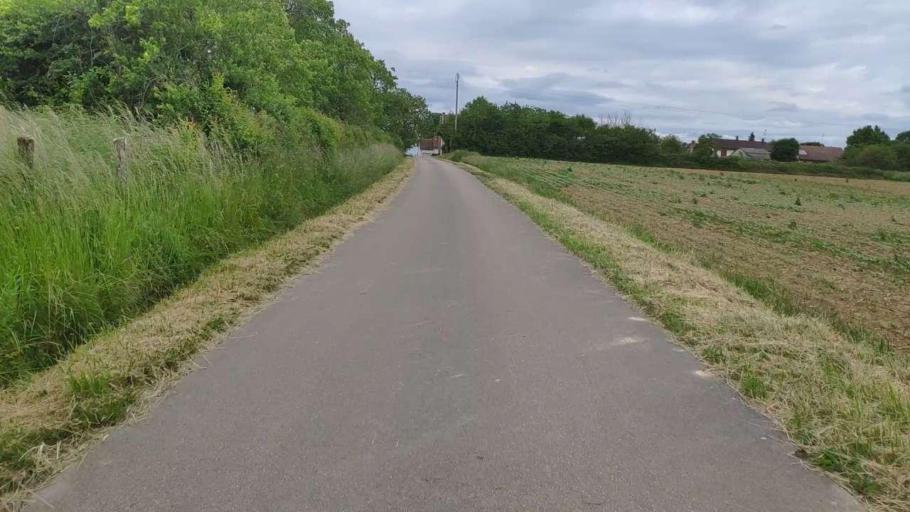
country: FR
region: Franche-Comte
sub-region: Departement du Jura
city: Bletterans
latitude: 46.7880
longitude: 5.5057
